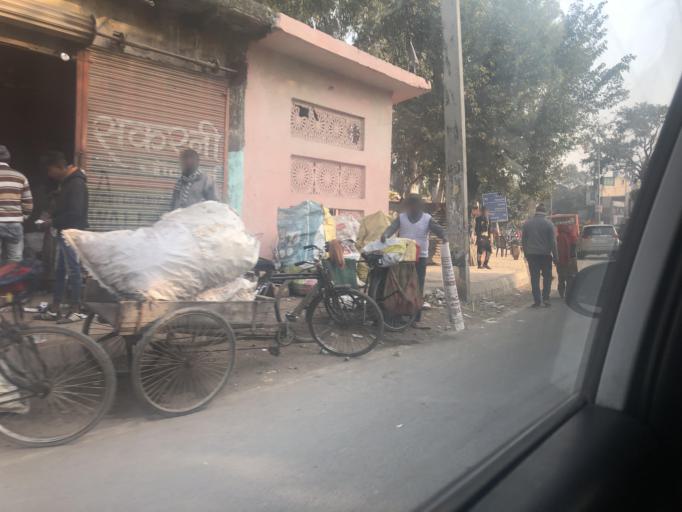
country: IN
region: Haryana
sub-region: Jhajjar
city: Bahadurgarh
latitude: 28.6166
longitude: 76.9754
